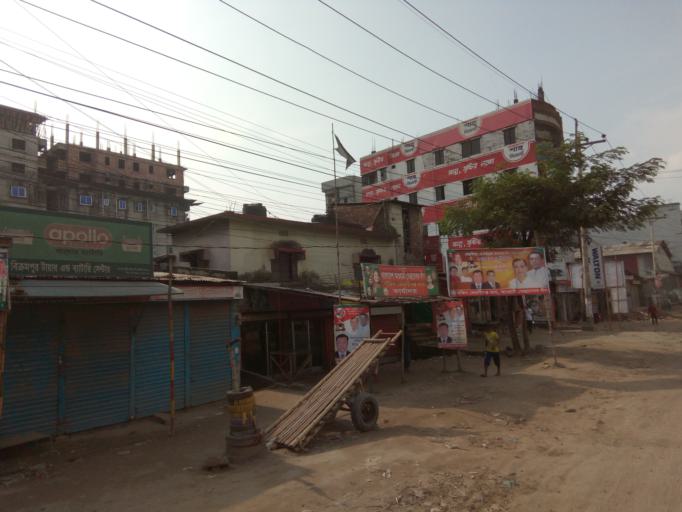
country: BD
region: Dhaka
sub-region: Dhaka
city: Dhaka
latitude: 23.6959
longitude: 90.3986
